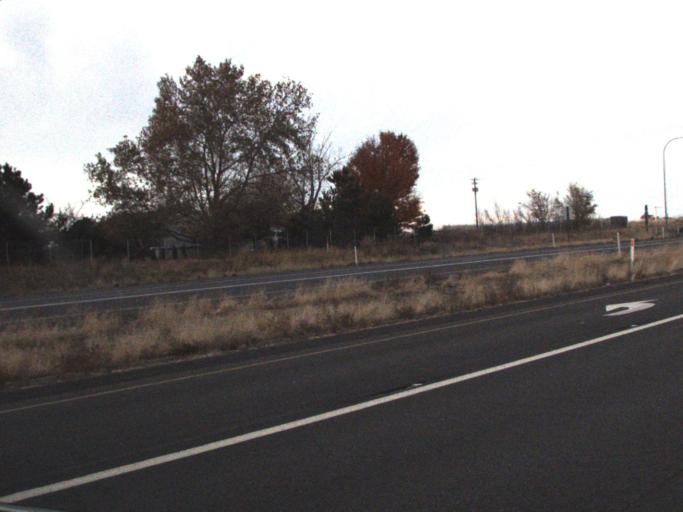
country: US
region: Washington
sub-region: Walla Walla County
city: Burbank
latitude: 46.1747
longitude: -118.9630
